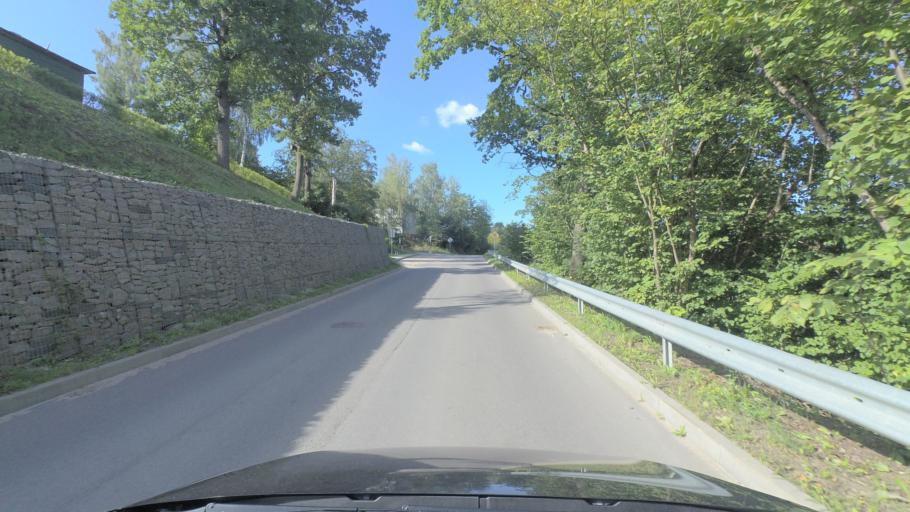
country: LT
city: Nemencine
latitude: 54.8495
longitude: 25.3736
